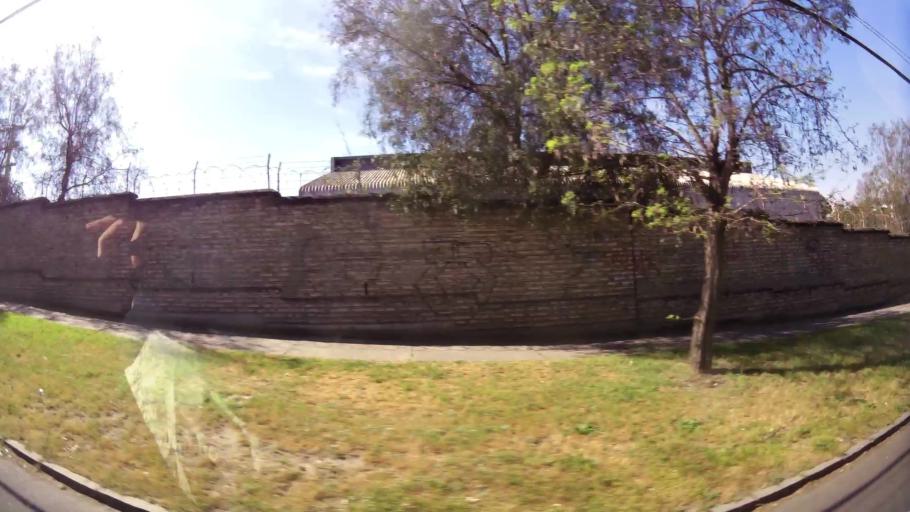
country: CL
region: Santiago Metropolitan
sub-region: Provincia de Santiago
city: Lo Prado
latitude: -33.4958
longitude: -70.7104
